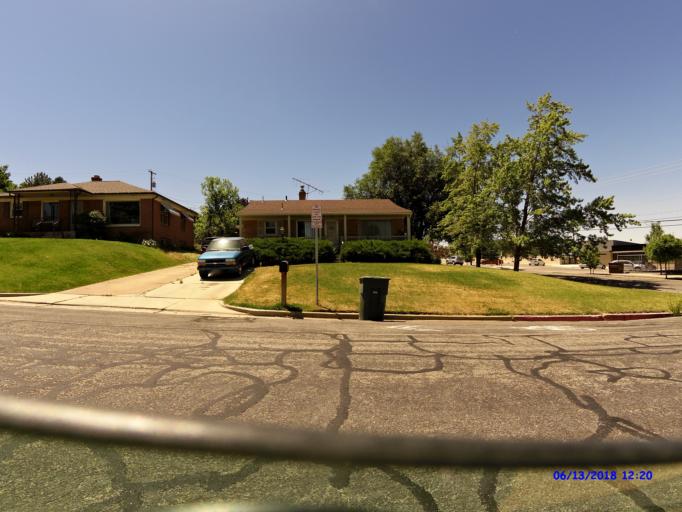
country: US
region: Utah
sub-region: Weber County
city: Ogden
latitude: 41.2119
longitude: -111.9454
